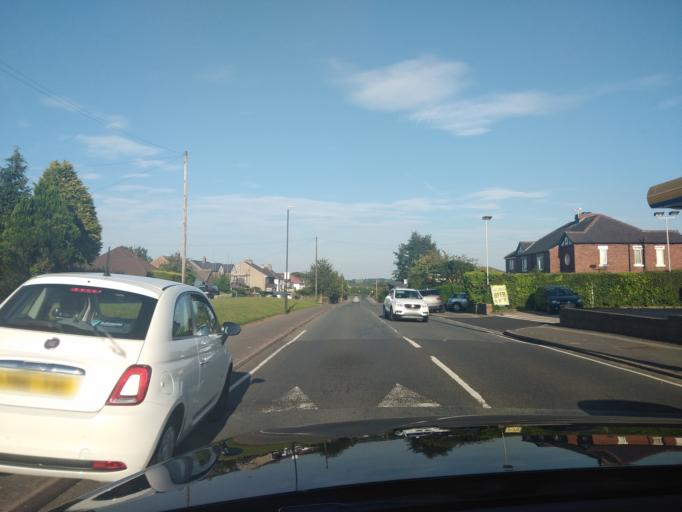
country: GB
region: England
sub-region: Derbyshire
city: Dronfield
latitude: 53.3057
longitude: -1.4920
